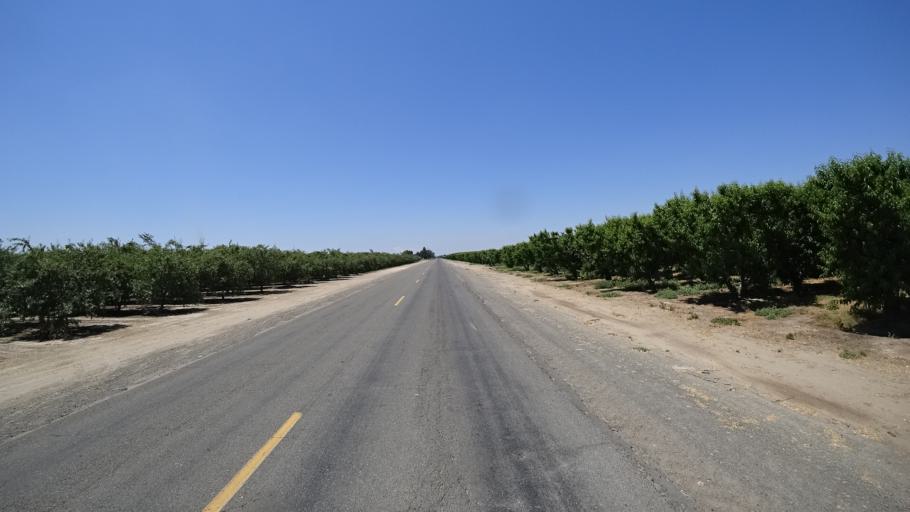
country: US
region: California
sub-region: Fresno County
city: Kingsburg
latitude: 36.4306
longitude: -119.5386
